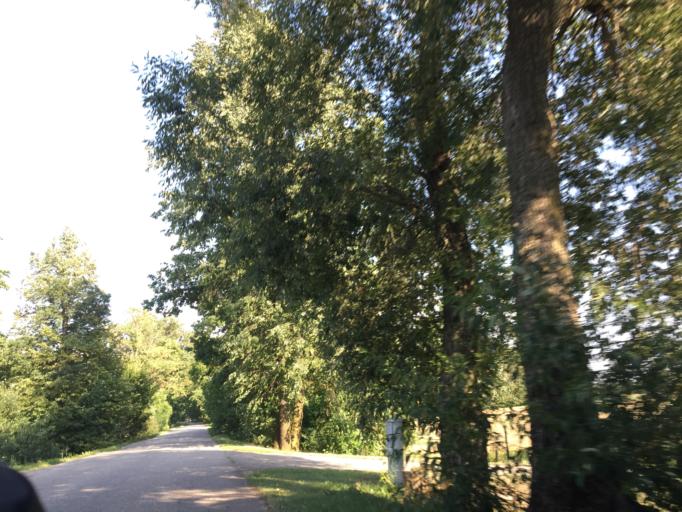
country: LT
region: Siauliu apskritis
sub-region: Joniskis
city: Joniskis
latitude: 56.4239
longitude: 23.6934
